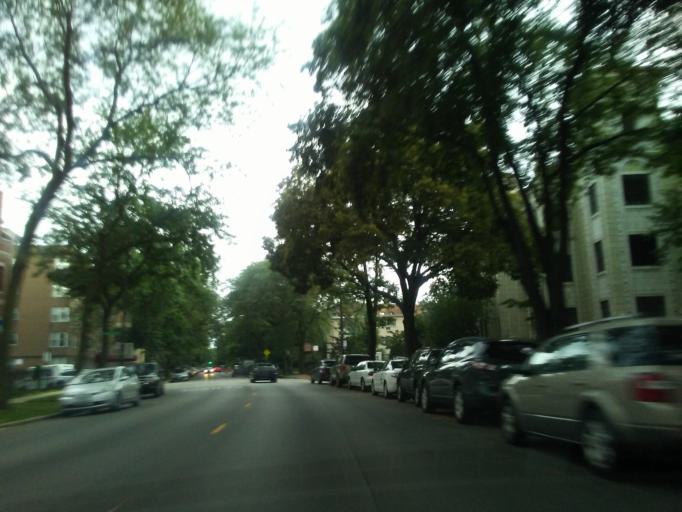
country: US
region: Illinois
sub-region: Cook County
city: Evanston
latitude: 42.0156
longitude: -87.6842
